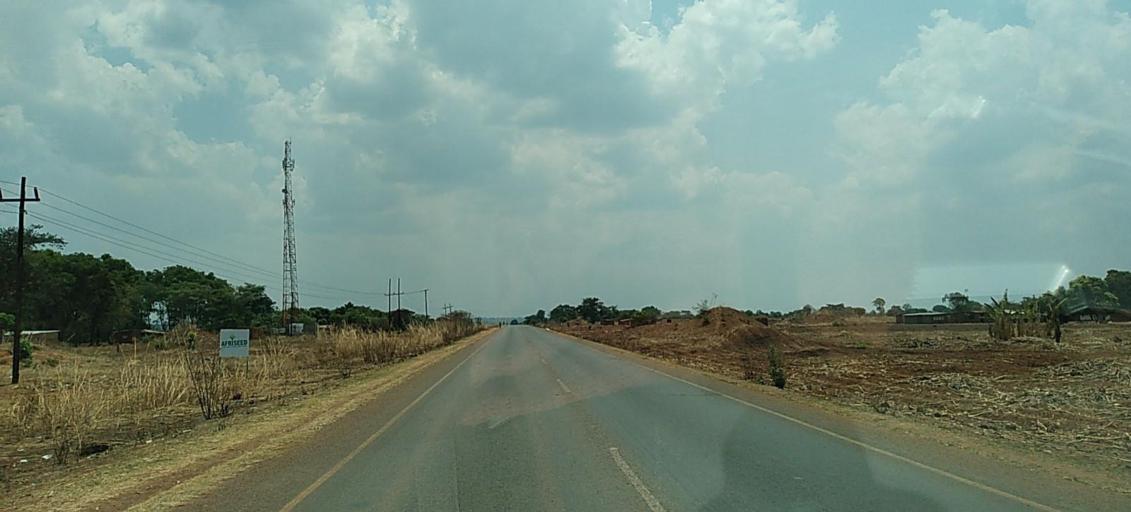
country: ZM
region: Copperbelt
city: Kalulushi
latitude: -12.8368
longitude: 27.9827
